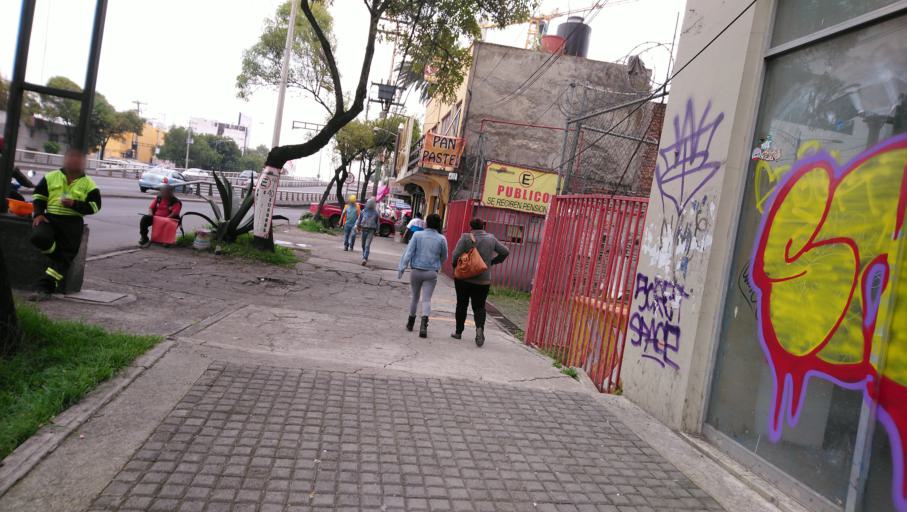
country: MX
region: Mexico City
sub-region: Iztacalco
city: Iztacalco
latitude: 19.4034
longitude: -99.1136
